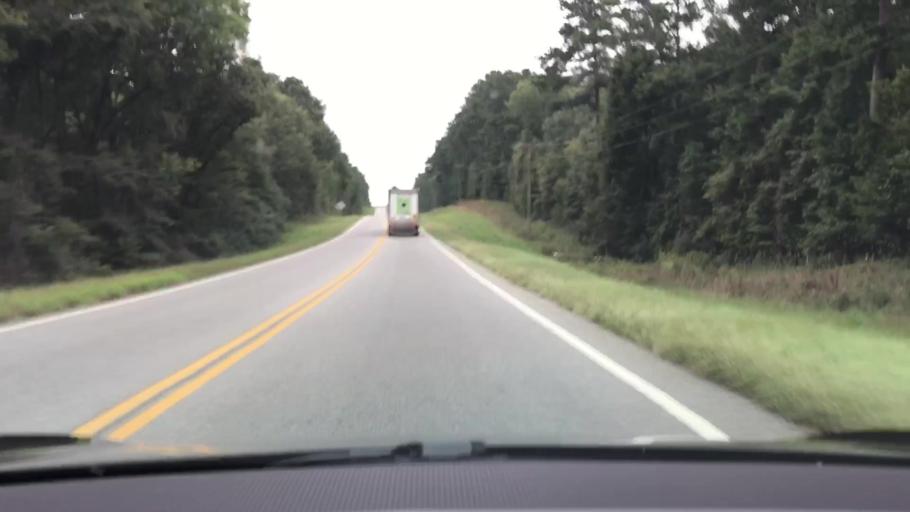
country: US
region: Georgia
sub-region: Greene County
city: Greensboro
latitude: 33.6549
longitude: -83.2376
